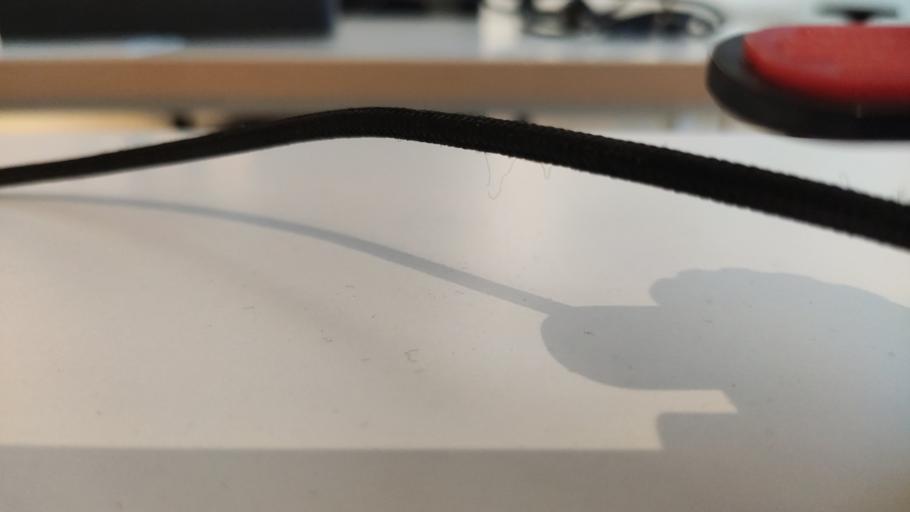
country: RU
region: Moskovskaya
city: Novopetrovskoye
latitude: 55.9107
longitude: 36.4421
